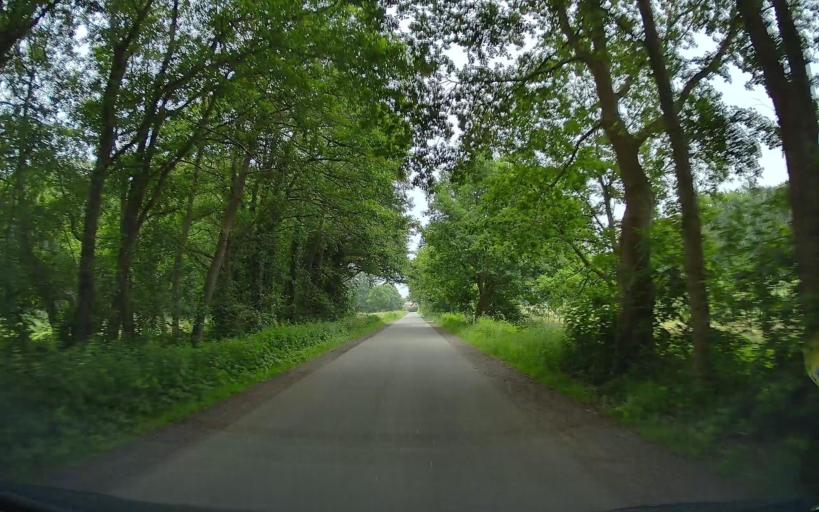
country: DE
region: Lower Saxony
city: Friesoythe
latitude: 53.0359
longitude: 7.8685
